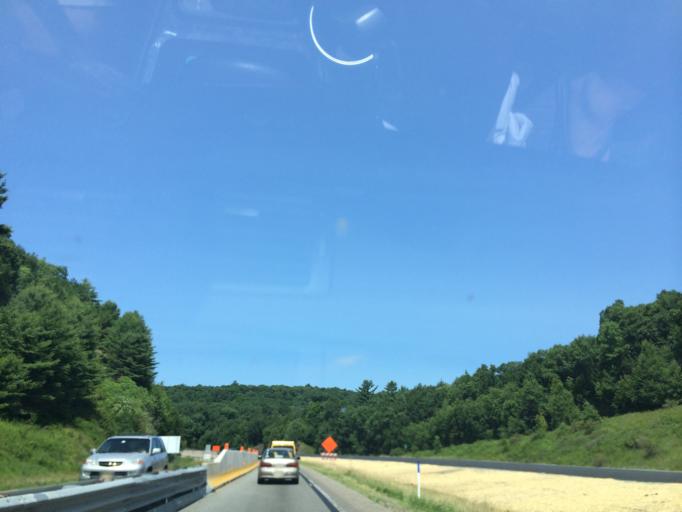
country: US
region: Pennsylvania
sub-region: Pike County
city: Milford
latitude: 41.3443
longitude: -74.7851
